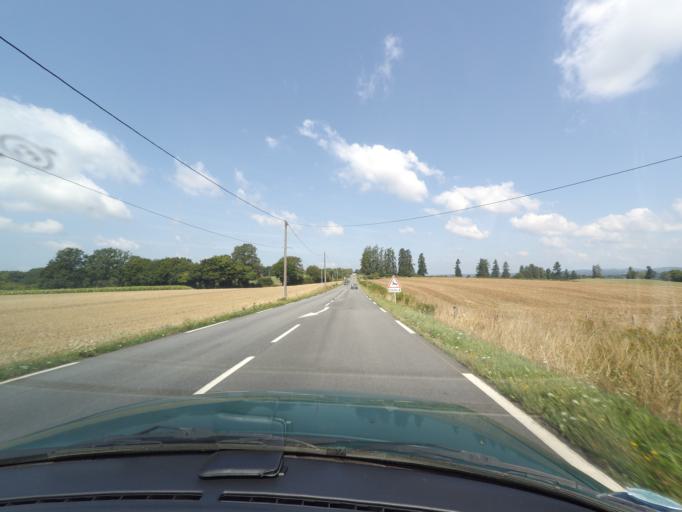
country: FR
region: Limousin
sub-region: Departement de la Haute-Vienne
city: Neuvic-Entier
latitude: 45.7543
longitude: 1.5941
